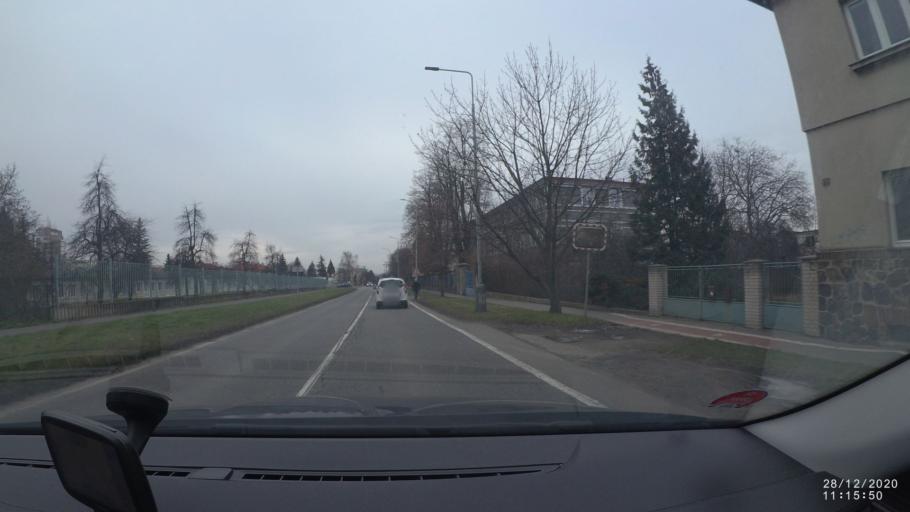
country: CZ
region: Praha
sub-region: Praha 18
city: Letnany
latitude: 50.1316
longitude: 14.5135
